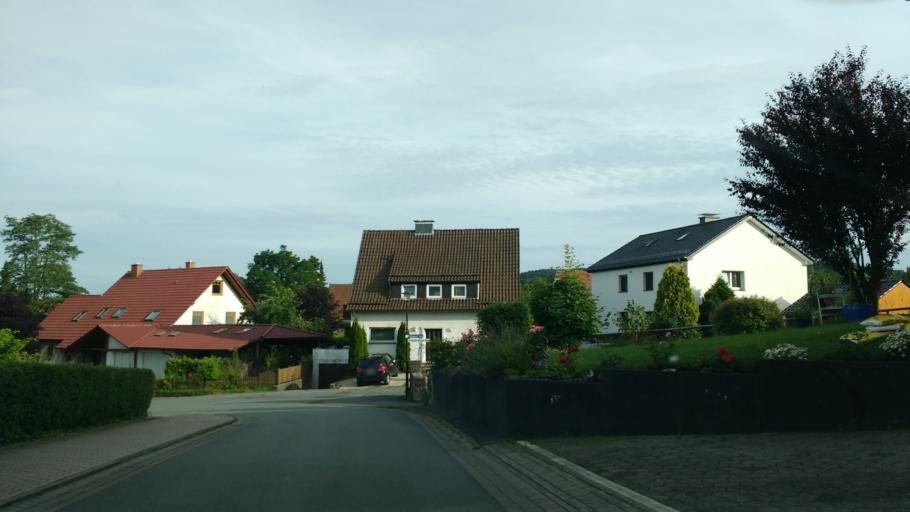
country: DE
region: North Rhine-Westphalia
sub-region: Regierungsbezirk Detmold
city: Horn
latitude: 51.8726
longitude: 8.9395
